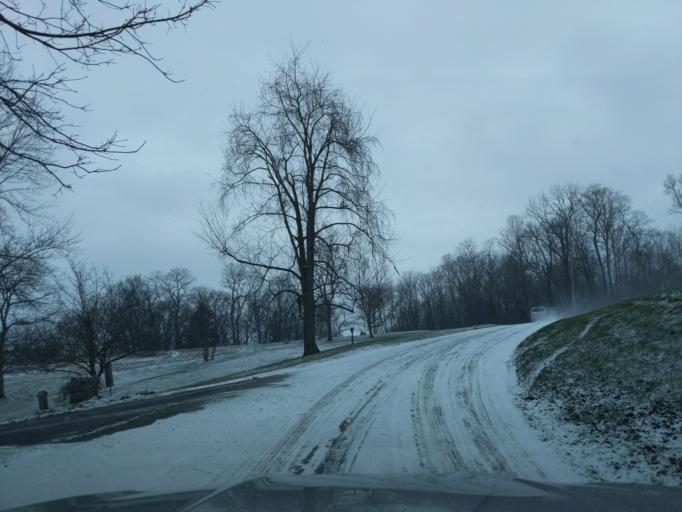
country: US
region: Indiana
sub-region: Decatur County
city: Westport
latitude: 39.2286
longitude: -85.5121
